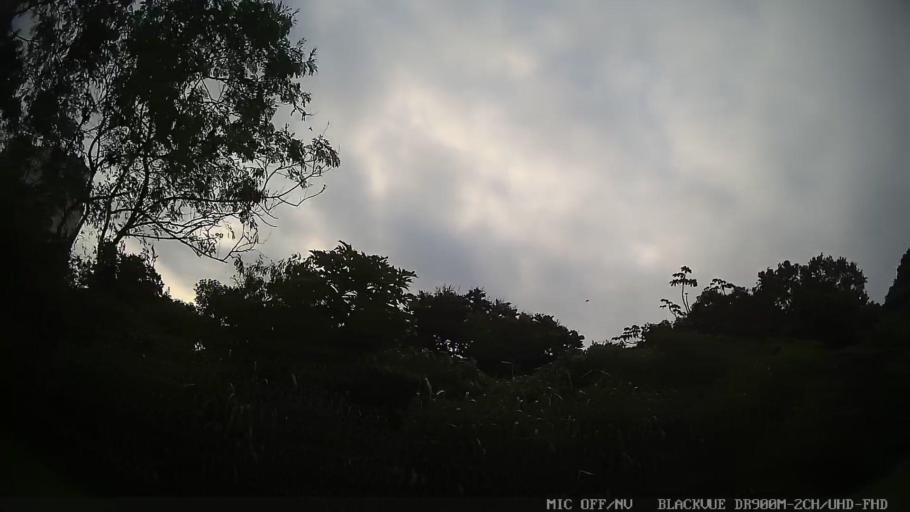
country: BR
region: Sao Paulo
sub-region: Guaruja
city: Guaruja
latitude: -23.9922
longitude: -46.1967
